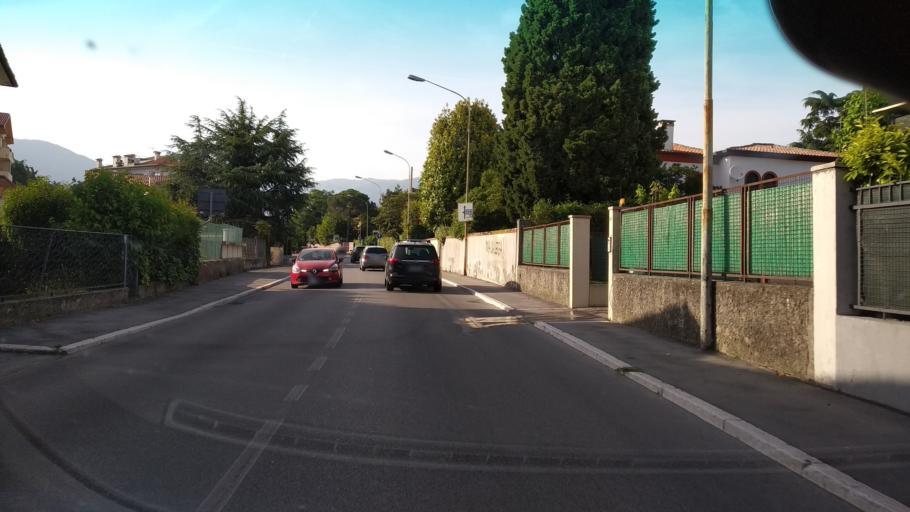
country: IT
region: Veneto
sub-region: Provincia di Vicenza
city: Bassano del Grappa
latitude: 45.7597
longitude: 11.7416
